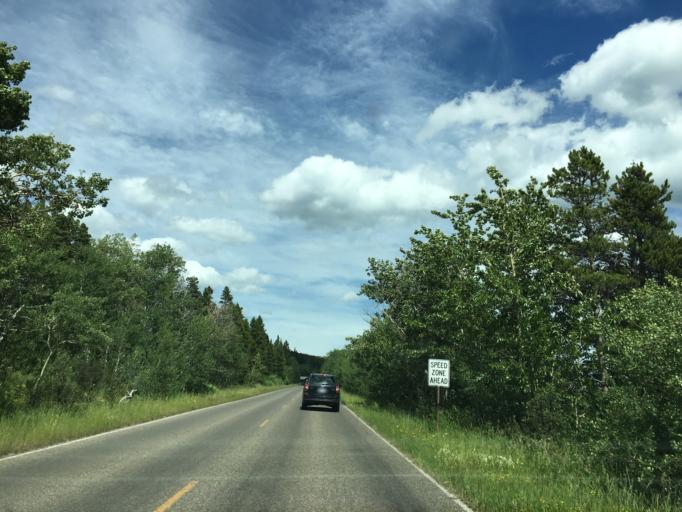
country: CA
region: Alberta
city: Cardston
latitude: 48.8203
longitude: -113.5839
